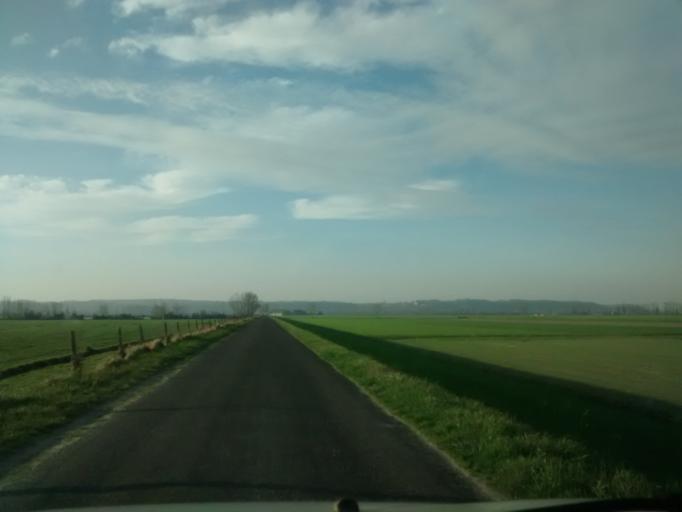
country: FR
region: Brittany
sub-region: Departement d'Ille-et-Vilaine
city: Roz-sur-Couesnon
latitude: 48.6086
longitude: -1.5556
